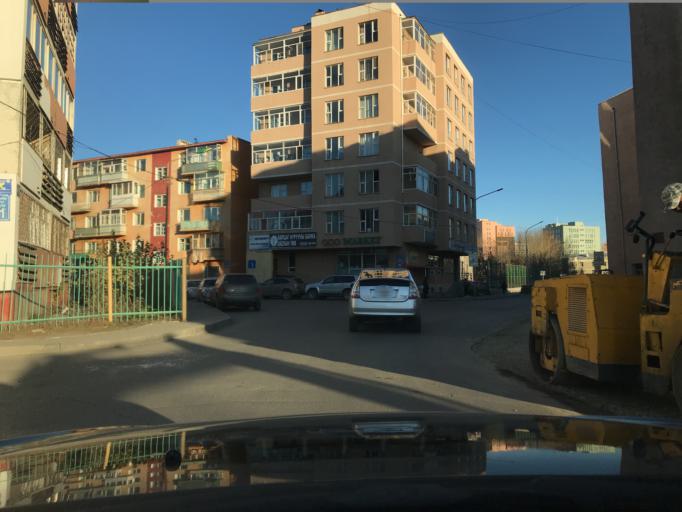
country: MN
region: Ulaanbaatar
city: Ulaanbaatar
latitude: 47.9255
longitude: 106.9090
